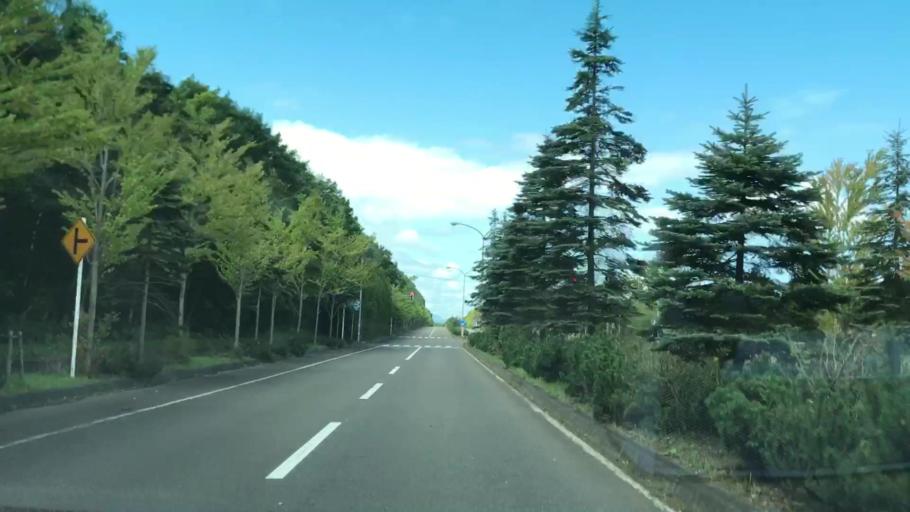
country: JP
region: Hokkaido
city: Chitose
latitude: 42.7745
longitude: 141.6005
